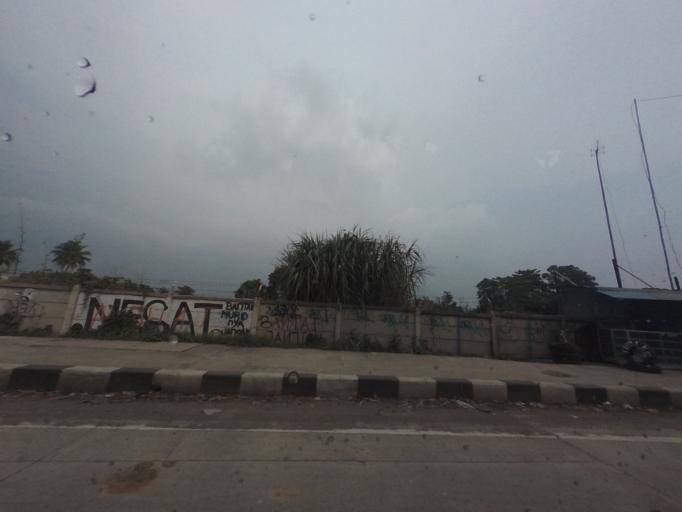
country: ID
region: West Java
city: Cicurug
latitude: -6.7538
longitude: 106.7995
